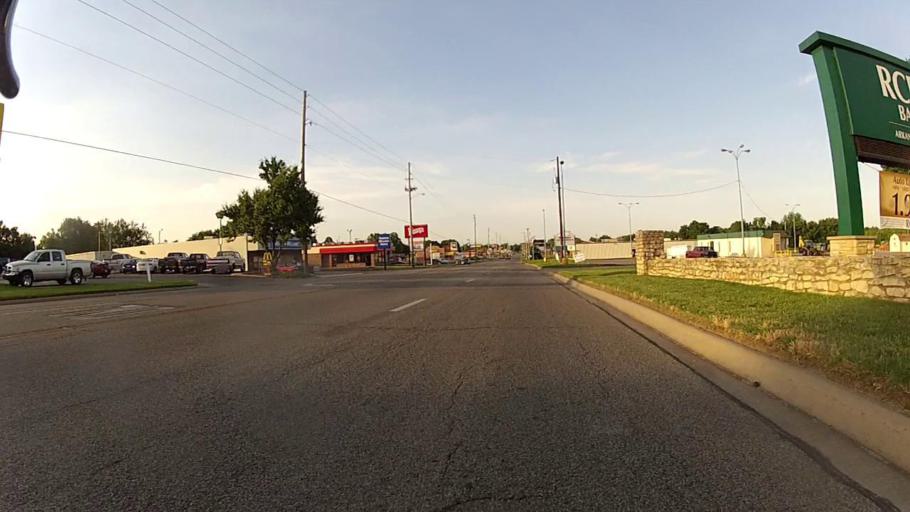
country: US
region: Kansas
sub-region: Cowley County
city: Arkansas City
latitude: 37.0849
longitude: -97.0403
